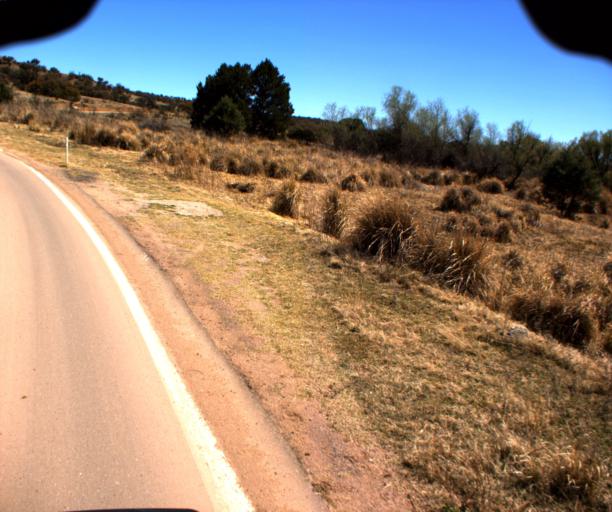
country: US
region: Arizona
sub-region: Cochise County
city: Huachuca City
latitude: 31.5421
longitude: -110.5130
